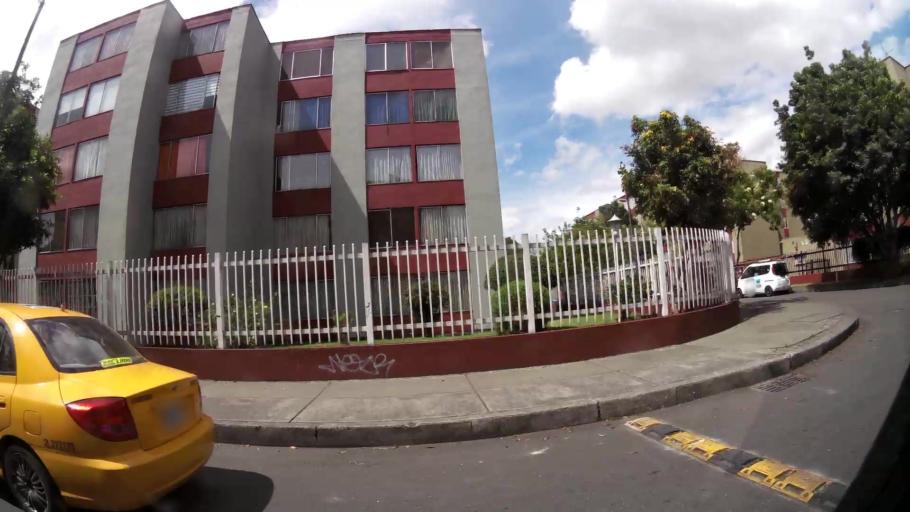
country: CO
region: Bogota D.C.
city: Bogota
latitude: 4.6970
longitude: -74.1090
